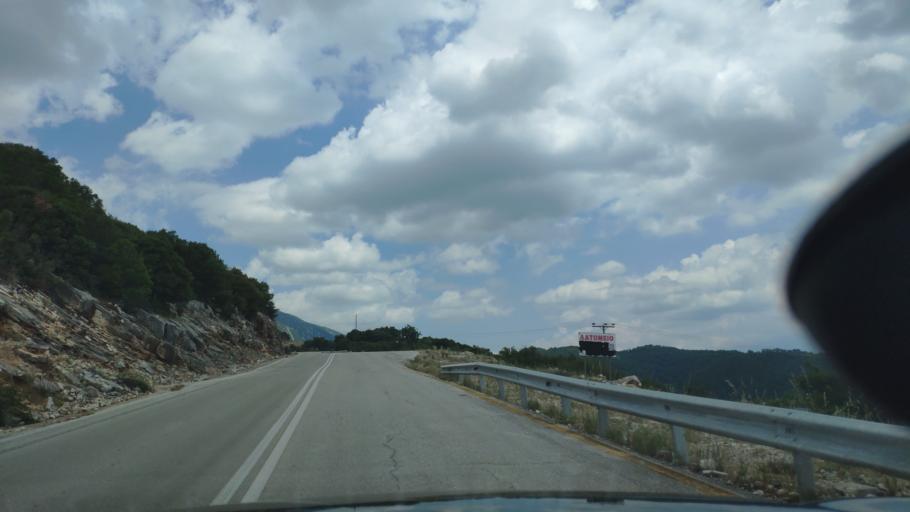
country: GR
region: Epirus
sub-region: Nomos Artas
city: Grammenitsa
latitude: 39.2792
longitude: 20.9761
